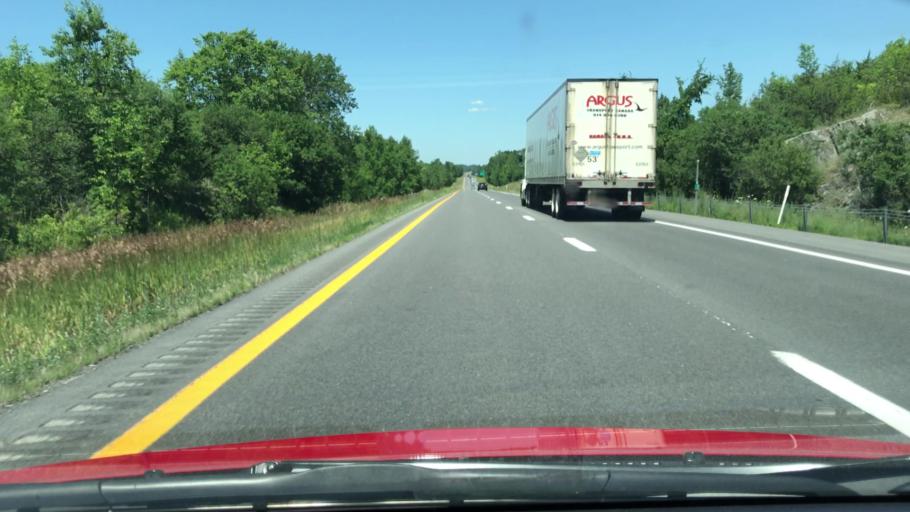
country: US
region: New York
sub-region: Clinton County
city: Cumberland Head
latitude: 44.7548
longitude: -73.4284
